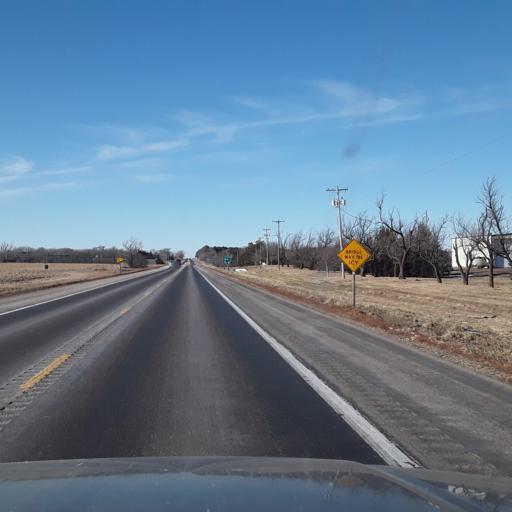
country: US
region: Nebraska
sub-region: Adams County
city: Hastings
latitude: 40.5680
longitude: -98.4325
